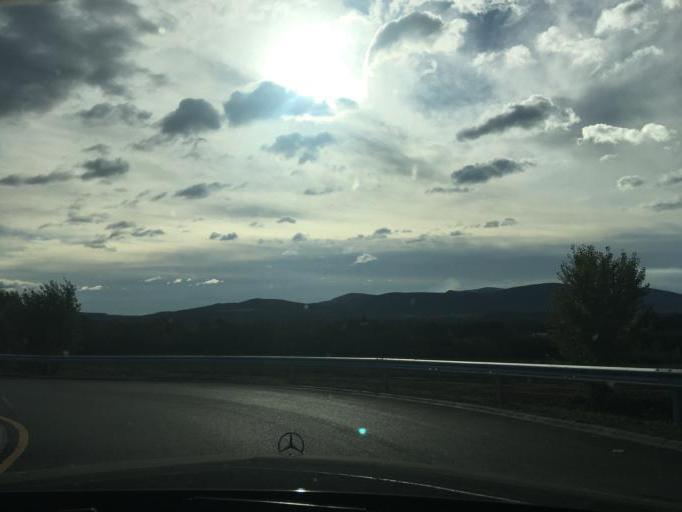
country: HU
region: Borsod-Abauj-Zemplen
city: Gonc
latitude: 48.5244
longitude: 21.2489
